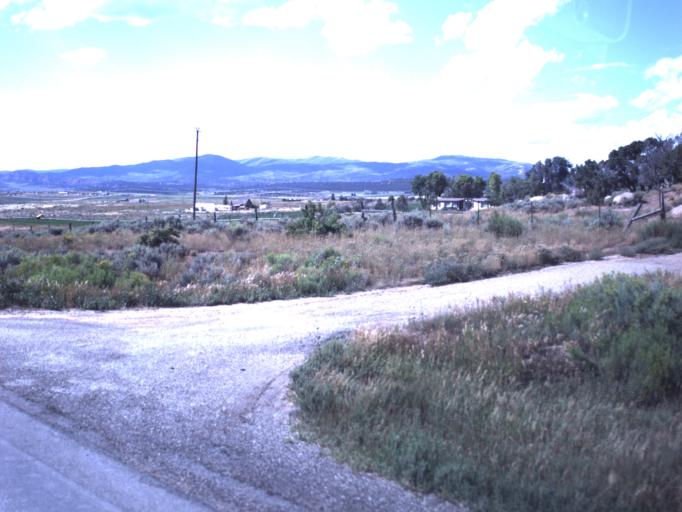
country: US
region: Utah
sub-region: Duchesne County
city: Duchesne
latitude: 40.2097
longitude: -110.8274
